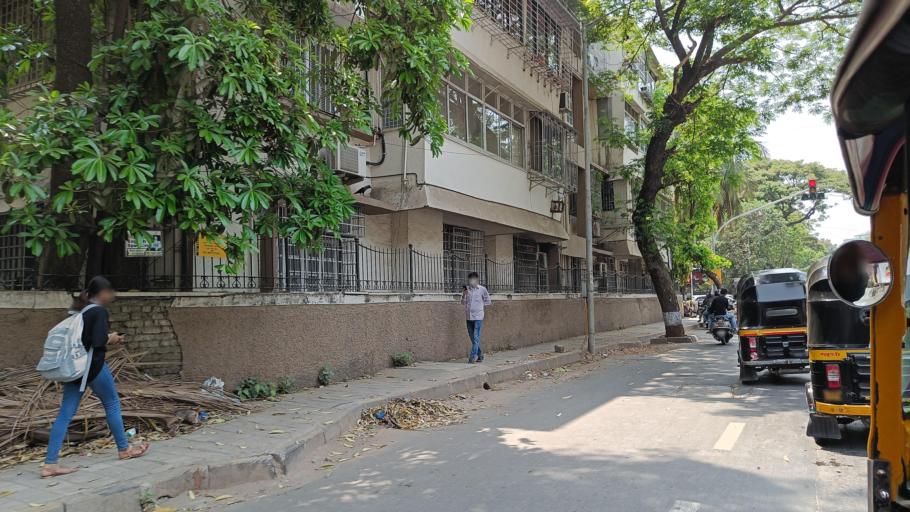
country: IN
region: Maharashtra
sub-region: Mumbai Suburban
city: Mumbai
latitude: 19.0790
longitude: 72.8344
